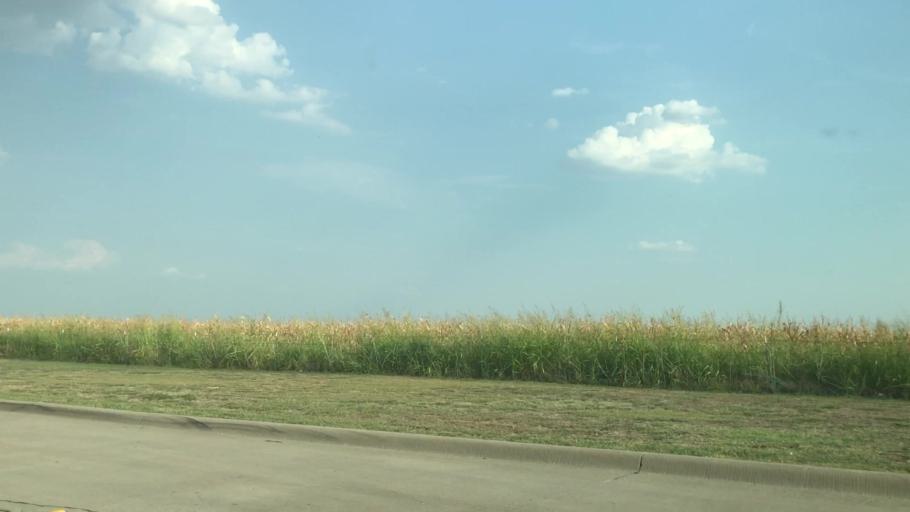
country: US
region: Texas
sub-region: Rockwall County
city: Rockwall
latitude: 32.9217
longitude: -96.4456
